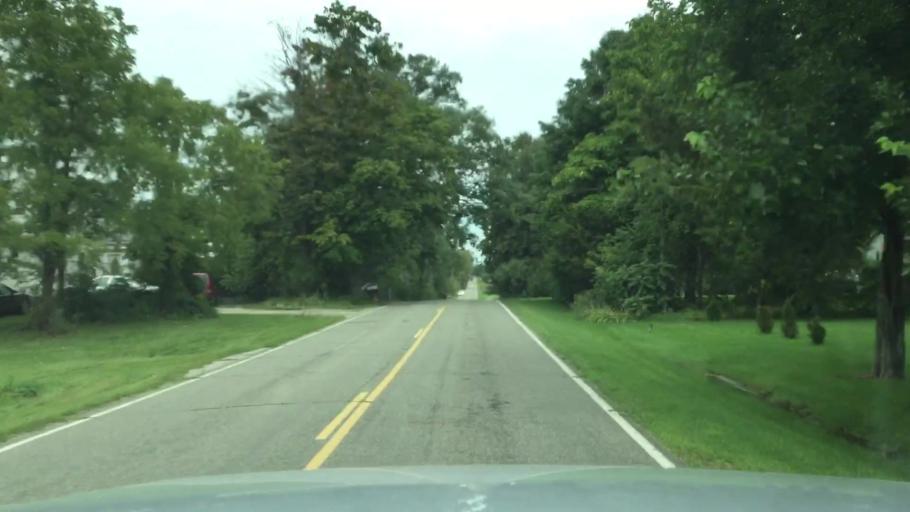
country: US
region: Michigan
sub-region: Shiawassee County
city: Durand
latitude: 42.9296
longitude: -83.9587
